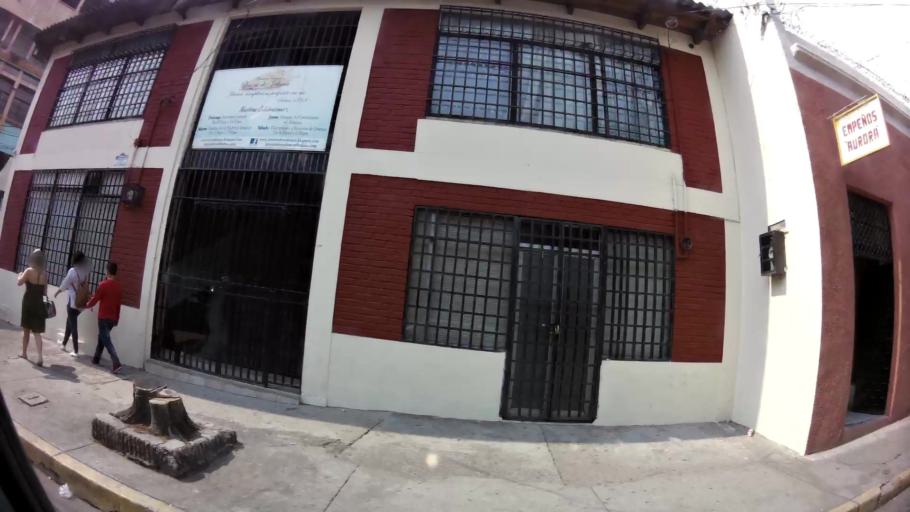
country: HN
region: Francisco Morazan
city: Tegucigalpa
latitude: 14.1068
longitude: -87.2025
